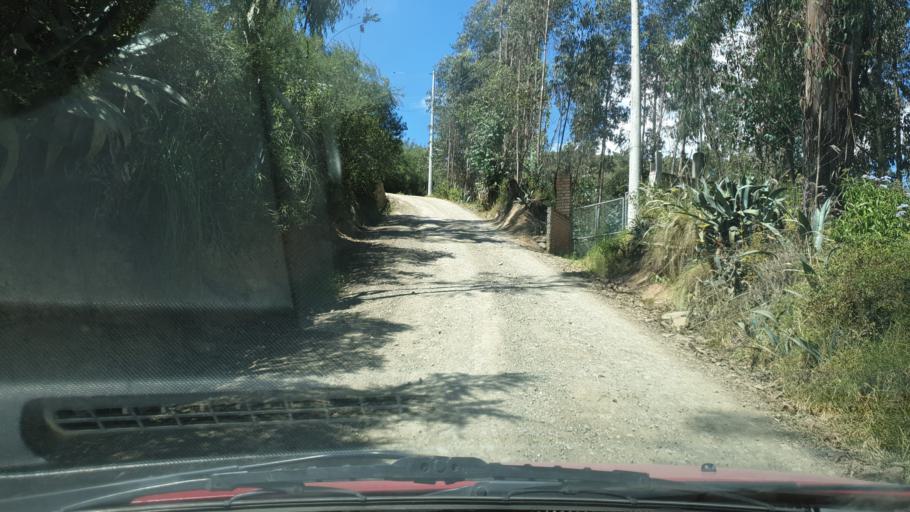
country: EC
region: Azuay
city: Llacao
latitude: -2.8769
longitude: -78.9063
